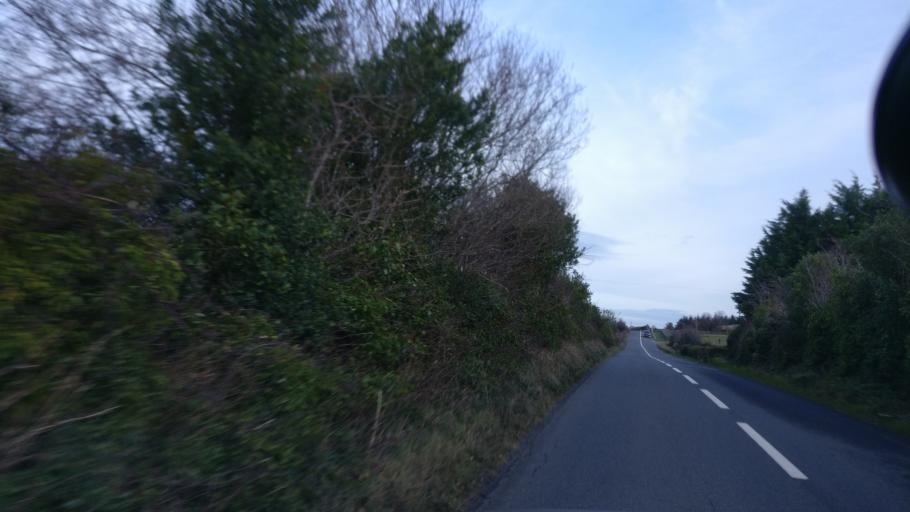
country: IE
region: Connaught
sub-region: County Galway
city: Oughterard
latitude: 53.5319
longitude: -9.3410
